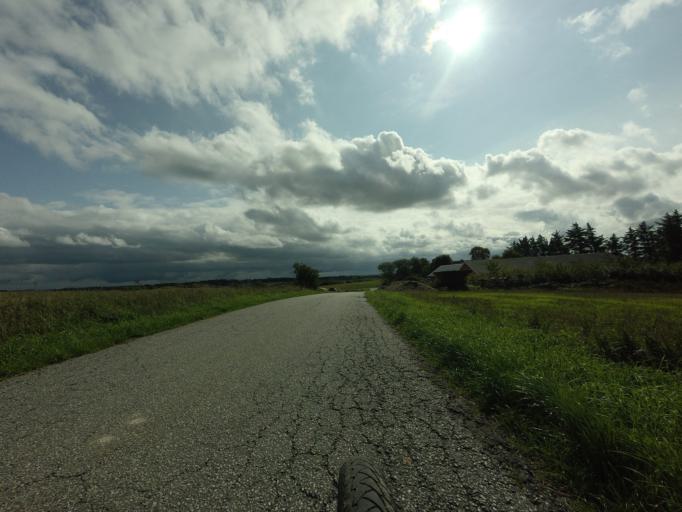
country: DK
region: North Denmark
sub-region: Hjorring Kommune
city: Hjorring
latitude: 57.5309
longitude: 10.0400
